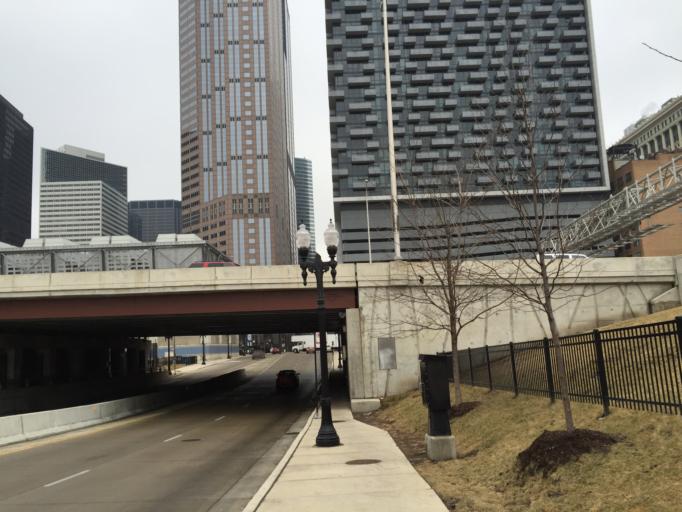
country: US
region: Illinois
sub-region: Cook County
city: Chicago
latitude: 41.8752
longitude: -87.6350
